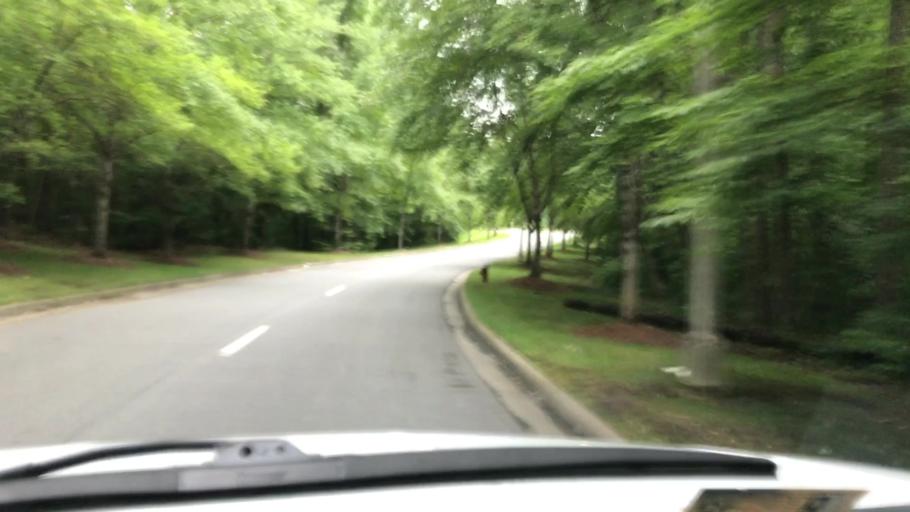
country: US
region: Virginia
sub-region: Henrico County
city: Short Pump
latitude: 37.6023
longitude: -77.6704
